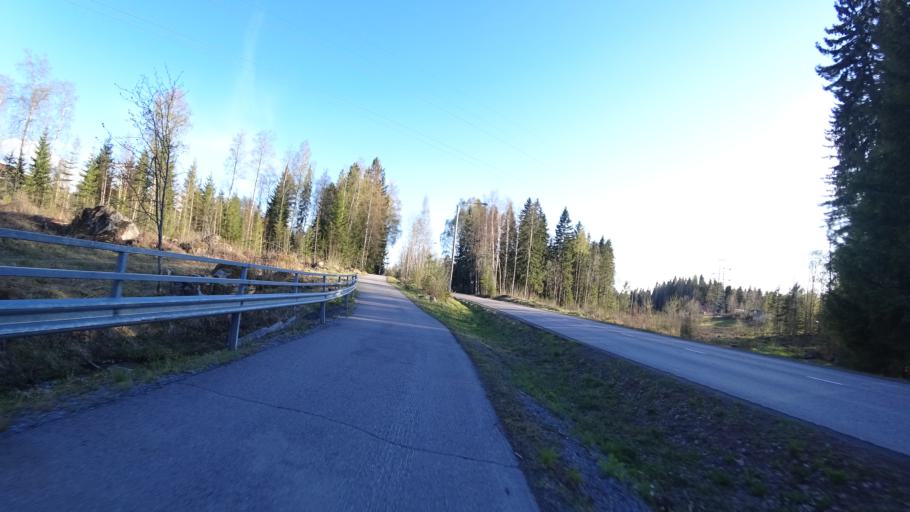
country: FI
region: Pirkanmaa
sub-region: Tampere
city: Yloejaervi
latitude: 61.5105
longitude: 23.5945
